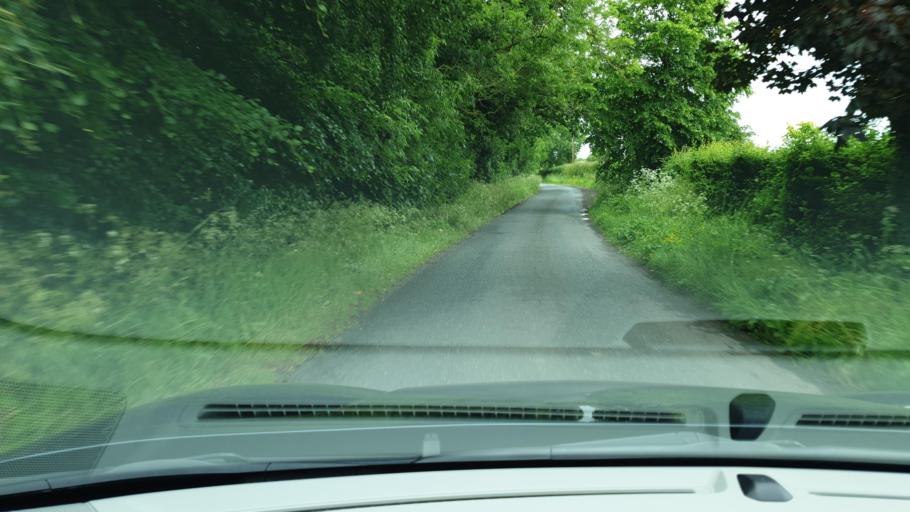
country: IE
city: Confey
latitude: 53.4065
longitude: -6.5246
